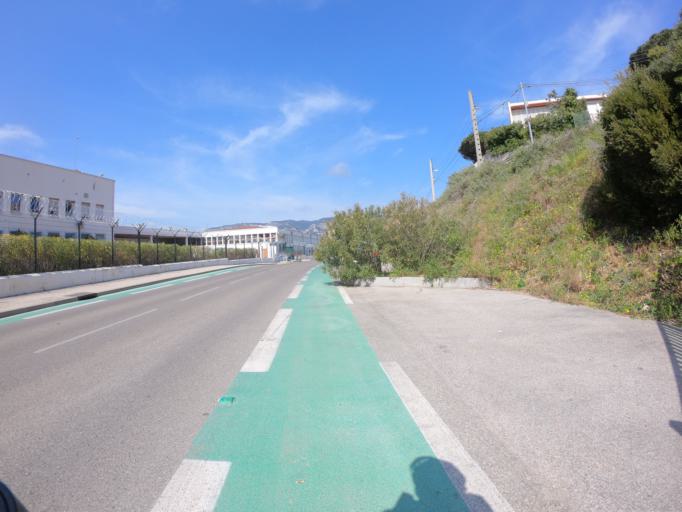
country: FR
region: Provence-Alpes-Cote d'Azur
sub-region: Departement du Var
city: Toulon
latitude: 43.1048
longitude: 5.9292
